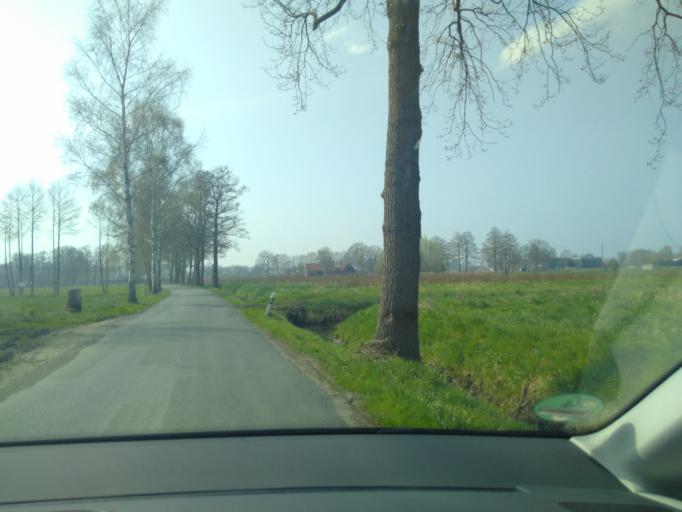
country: DE
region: North Rhine-Westphalia
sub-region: Regierungsbezirk Detmold
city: Verl
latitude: 51.8637
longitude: 8.4819
